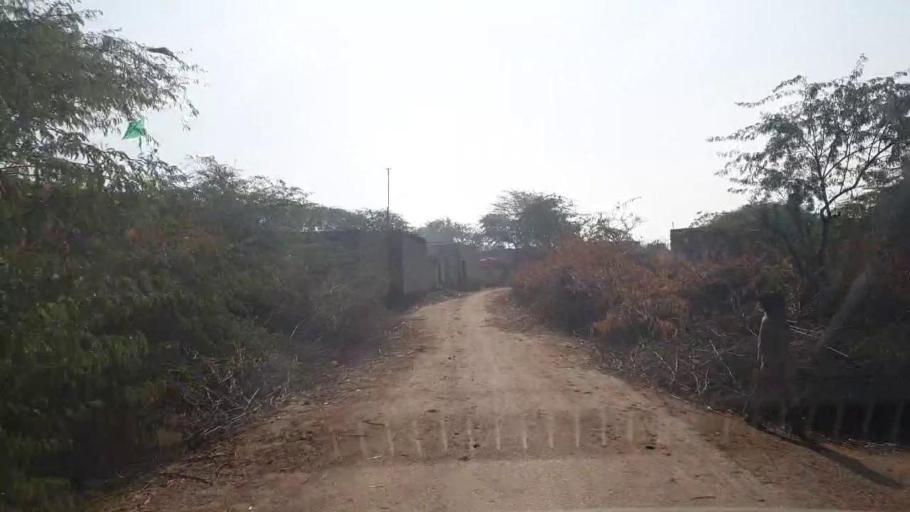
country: PK
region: Sindh
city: Shahdadpur
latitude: 25.9638
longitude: 68.5789
